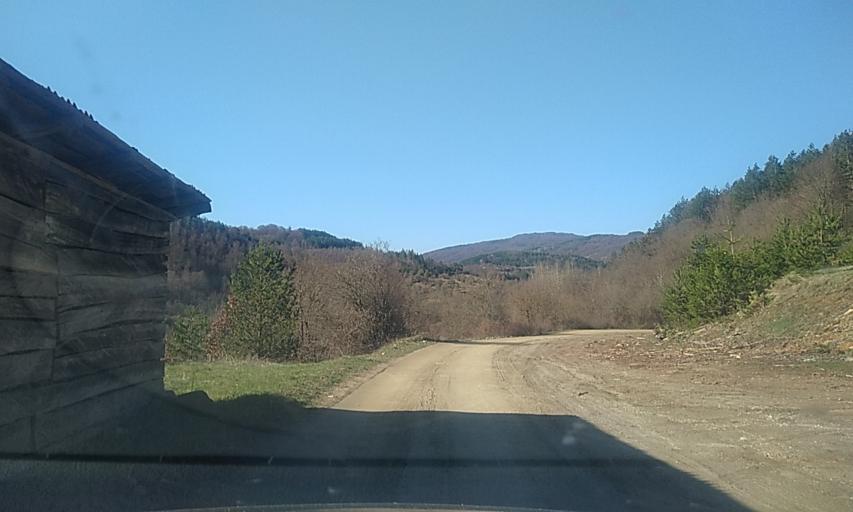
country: RS
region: Central Serbia
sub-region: Pcinjski Okrug
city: Bosilegrad
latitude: 42.3702
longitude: 22.4376
